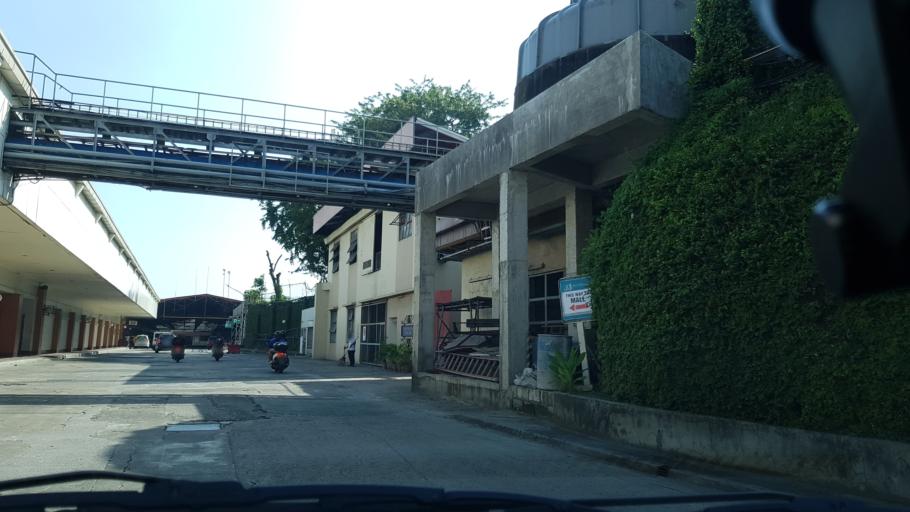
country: PH
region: Metro Manila
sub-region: Marikina
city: Calumpang
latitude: 14.6320
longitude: 121.0817
